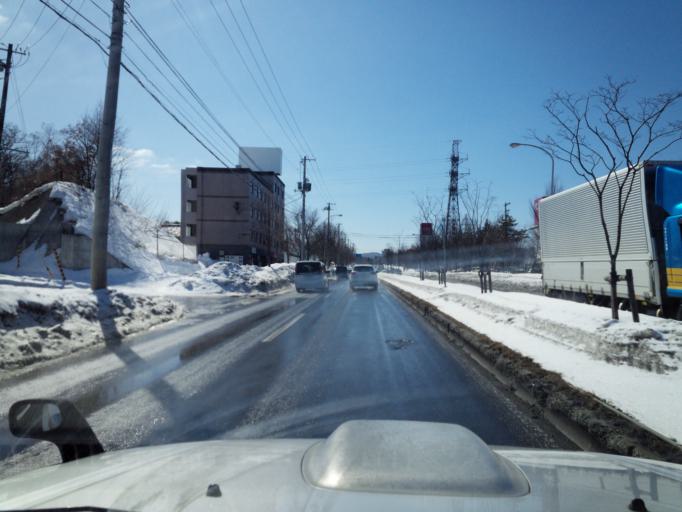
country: JP
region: Hokkaido
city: Kitahiroshima
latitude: 42.9968
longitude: 141.4600
